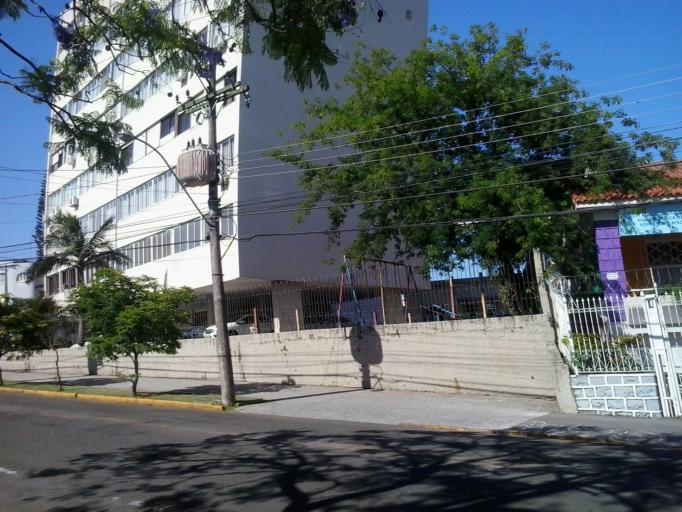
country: BR
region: Rio Grande do Sul
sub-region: Santa Maria
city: Santa Maria
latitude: -29.6868
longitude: -53.8008
